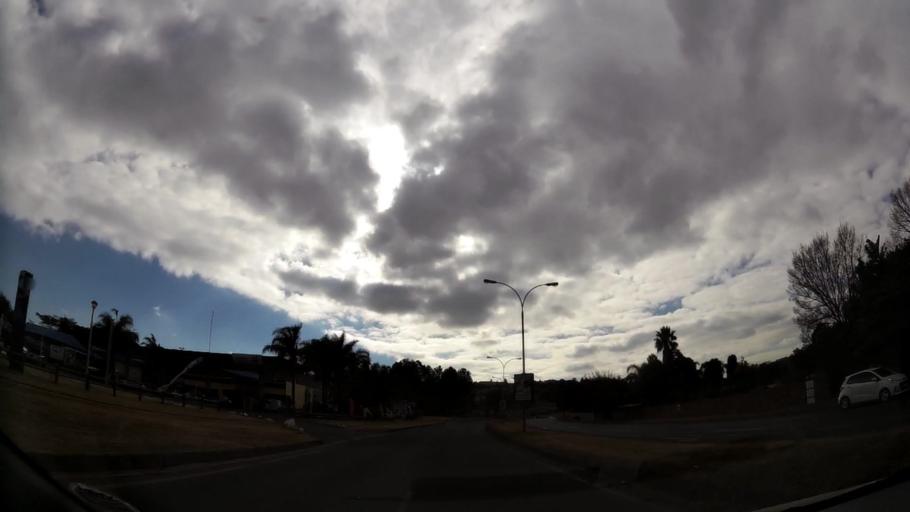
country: ZA
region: Gauteng
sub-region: City of Johannesburg Metropolitan Municipality
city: Roodepoort
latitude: -26.1090
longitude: 27.8558
